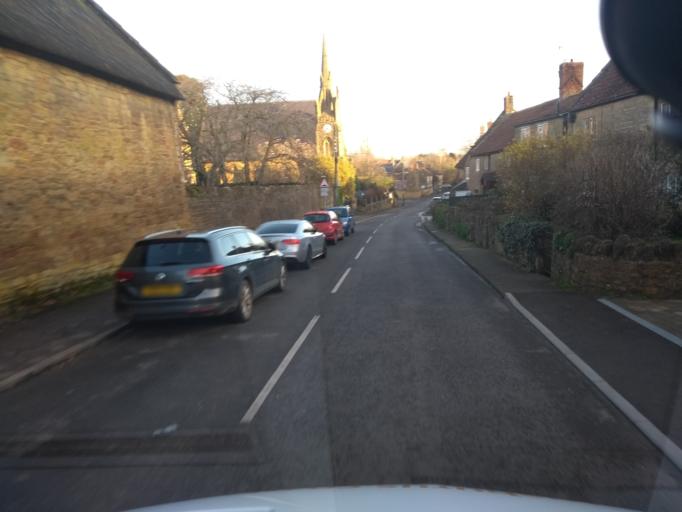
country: GB
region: England
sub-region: Somerset
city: Stoke-sub-Hamdon
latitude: 50.9541
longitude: -2.7507
